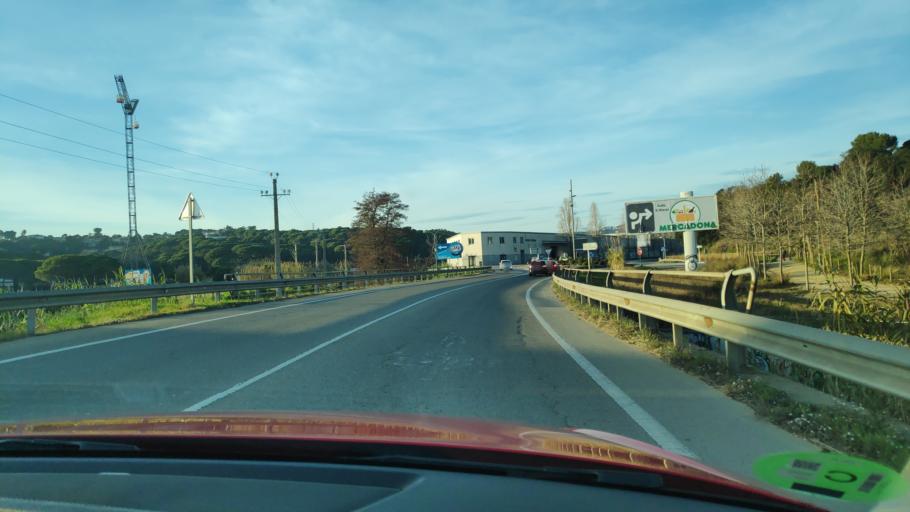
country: ES
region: Catalonia
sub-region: Provincia de Girona
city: Lloret de Mar
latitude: 41.7082
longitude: 2.8331
